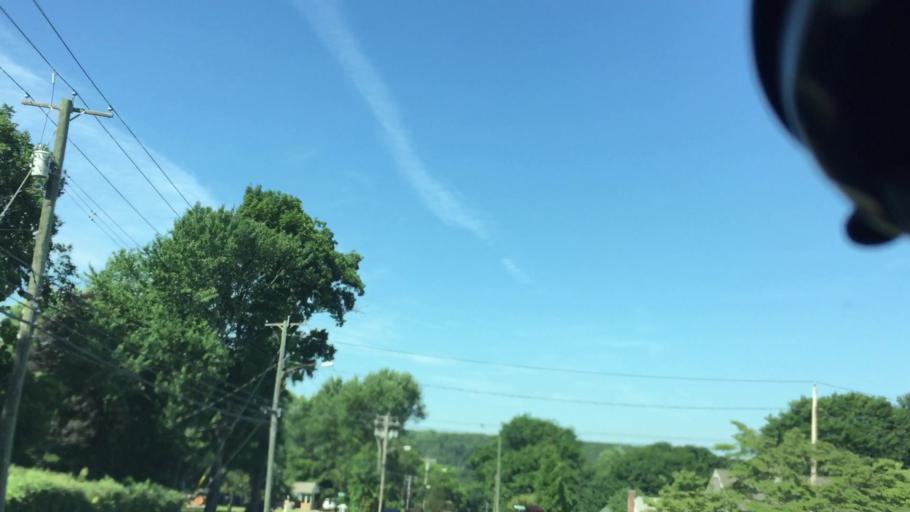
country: US
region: Connecticut
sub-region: Fairfield County
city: Trumbull
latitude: 41.2455
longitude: -73.2037
